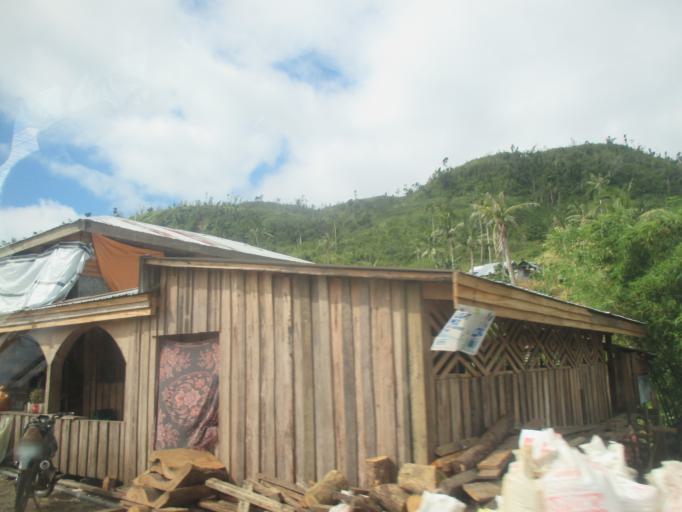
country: PH
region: Eastern Visayas
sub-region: Province of Eastern Samar
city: Lawa-an
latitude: 11.1153
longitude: 125.2447
